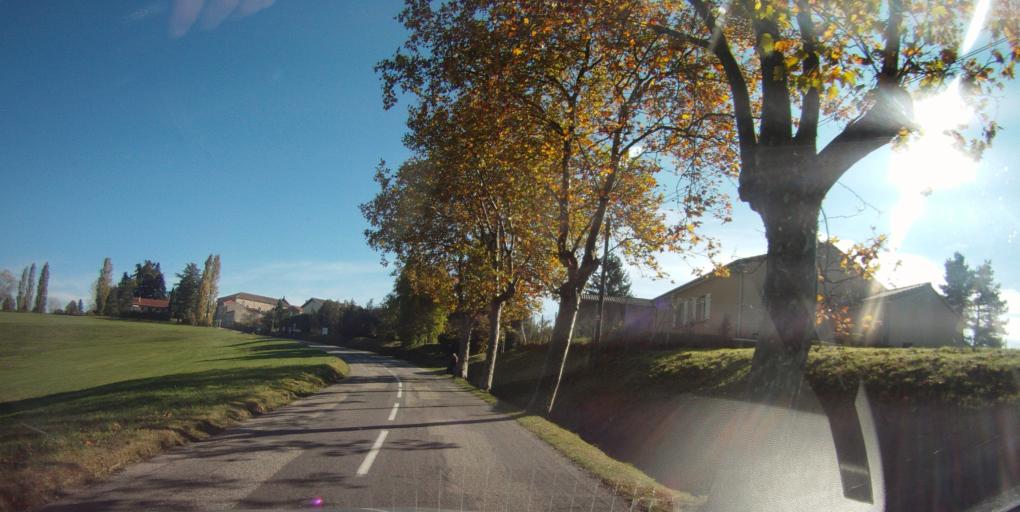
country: FR
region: Rhone-Alpes
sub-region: Departement de l'Ardeche
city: Vernoux-en-Vivarais
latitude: 44.8979
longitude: 4.6403
